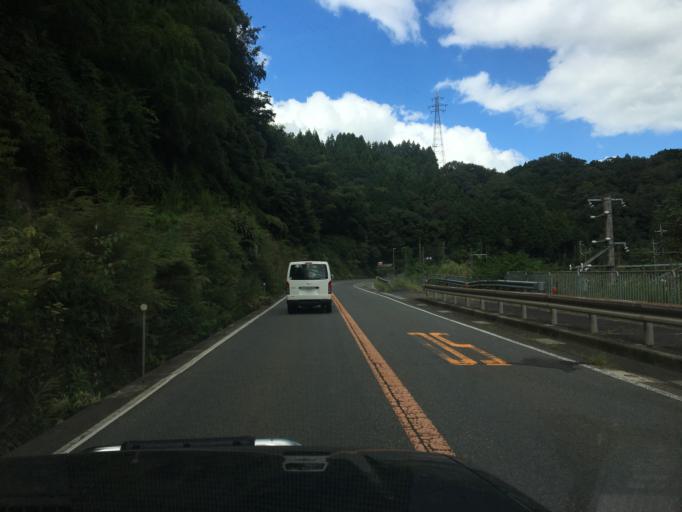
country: JP
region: Kyoto
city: Fukuchiyama
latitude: 35.3335
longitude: 134.9131
